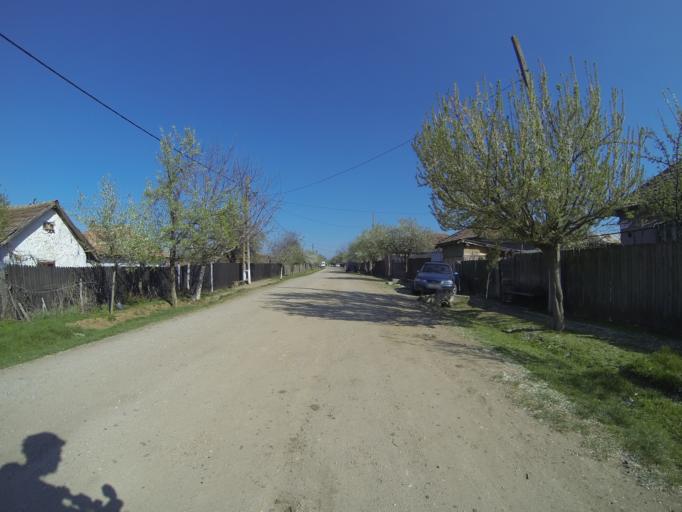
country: RO
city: Varvoru
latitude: 44.2257
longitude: 23.6186
